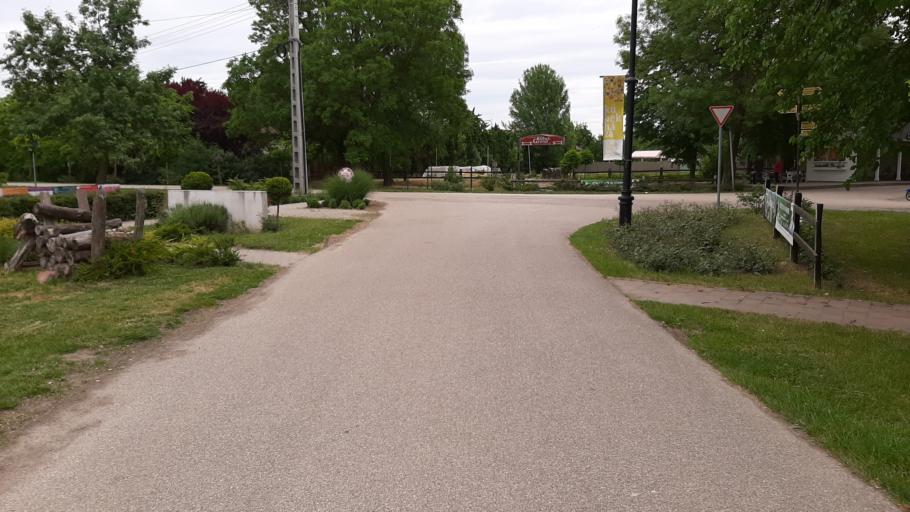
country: RO
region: Timis
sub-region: Comuna Beba Veche
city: Beba Veche
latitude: 46.1503
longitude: 20.2762
